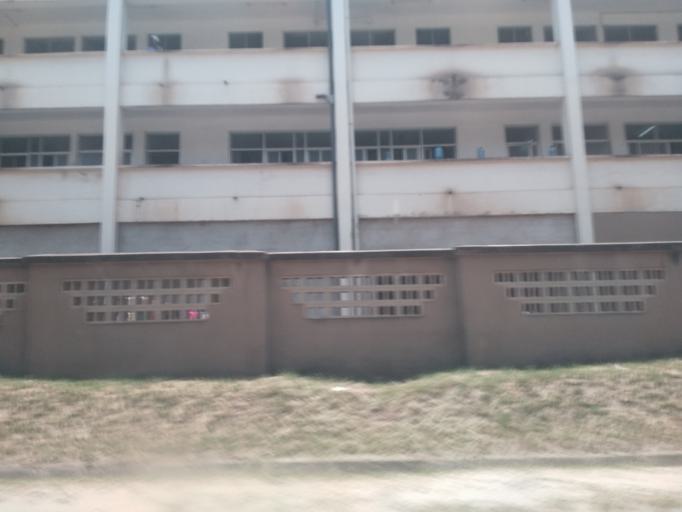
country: TZ
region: Dar es Salaam
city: Dar es Salaam
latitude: -6.8031
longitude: 39.2745
